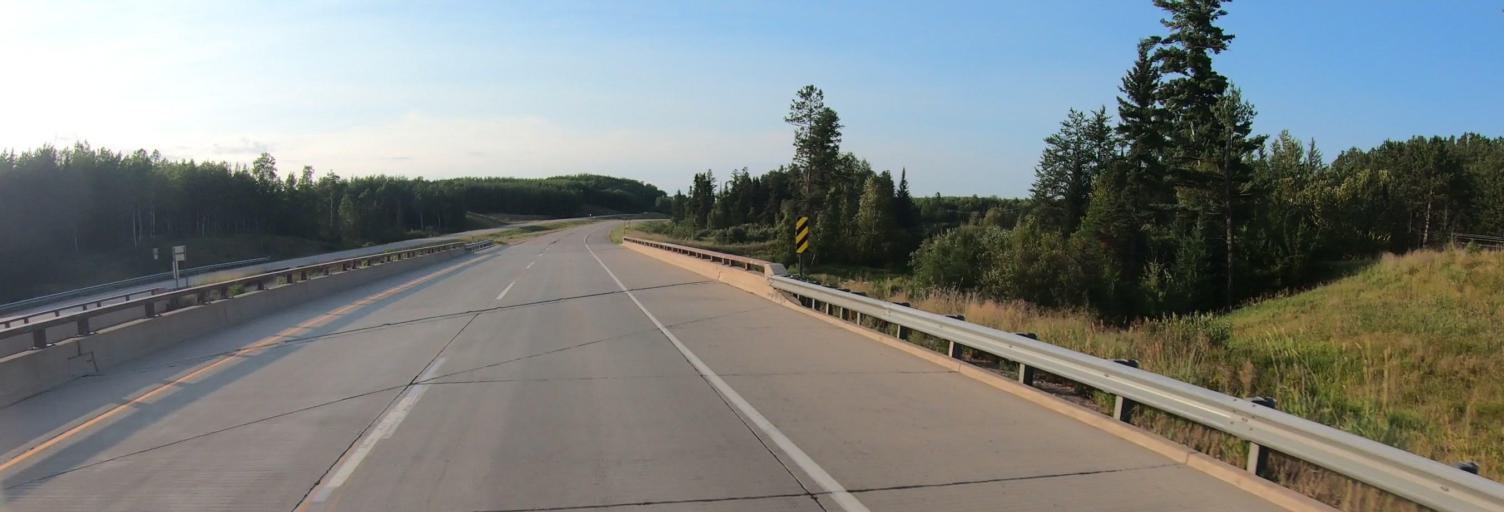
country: US
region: Minnesota
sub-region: Saint Louis County
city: Mountain Iron
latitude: 47.6779
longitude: -92.6357
